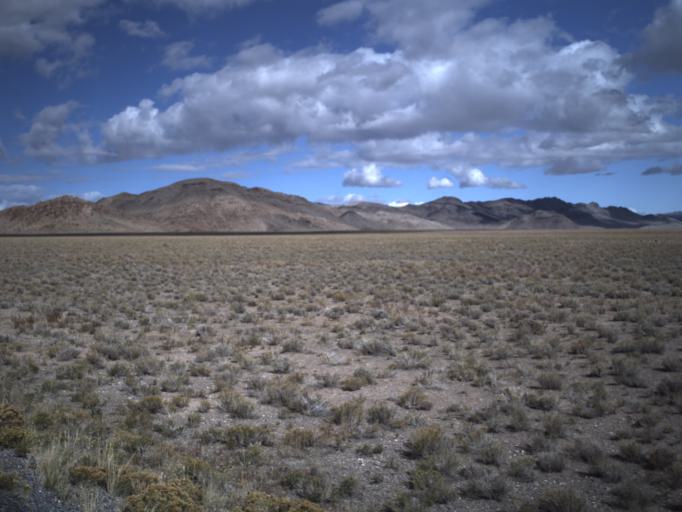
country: US
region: Utah
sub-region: Beaver County
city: Milford
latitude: 38.5707
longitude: -113.7858
